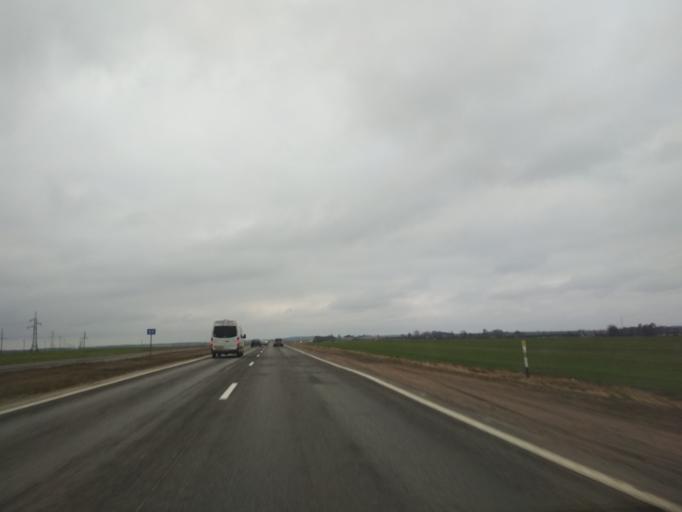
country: BY
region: Minsk
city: Blon'
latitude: 53.5818
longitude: 28.1182
